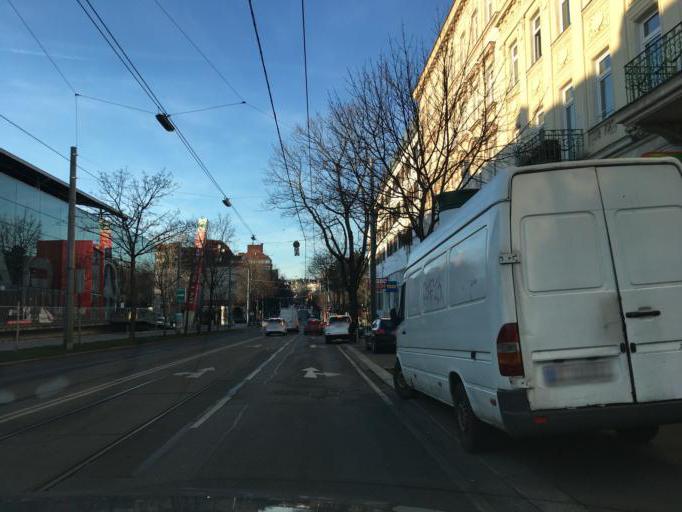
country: AT
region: Vienna
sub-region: Wien Stadt
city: Vienna
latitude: 48.2194
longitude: 16.3075
